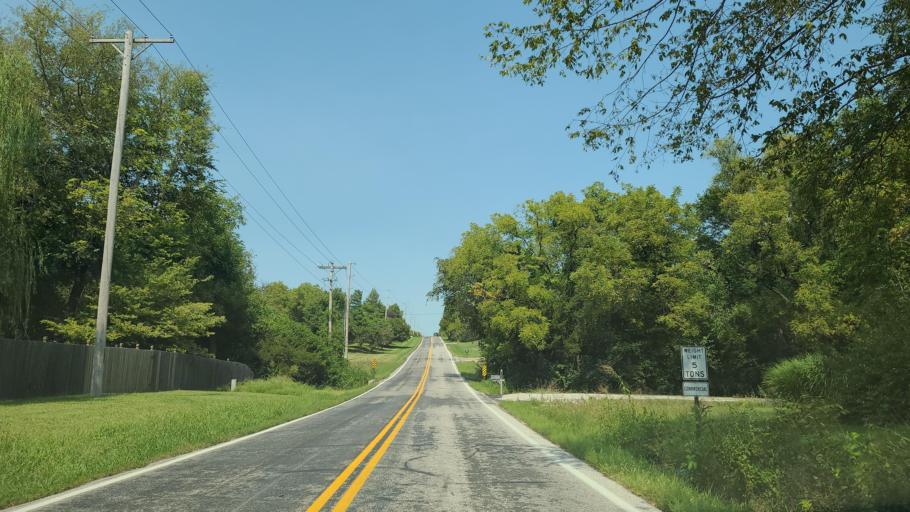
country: US
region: Kansas
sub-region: Douglas County
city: Lawrence
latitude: 38.9780
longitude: -95.2976
